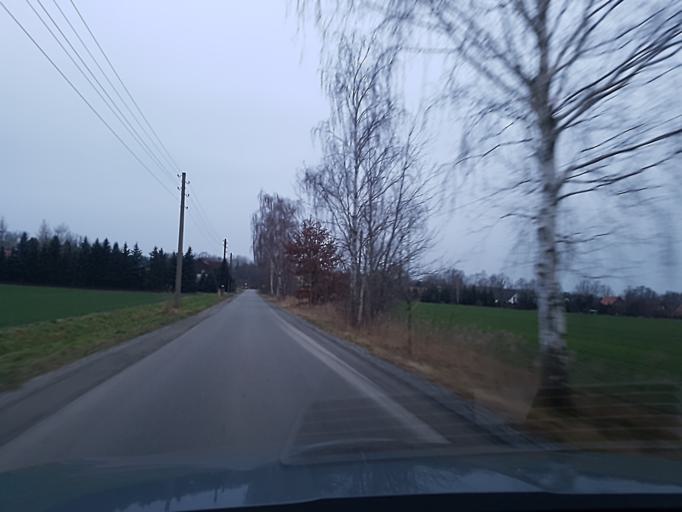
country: DE
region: Brandenburg
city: Schonewalde
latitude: 51.6396
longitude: 13.6109
